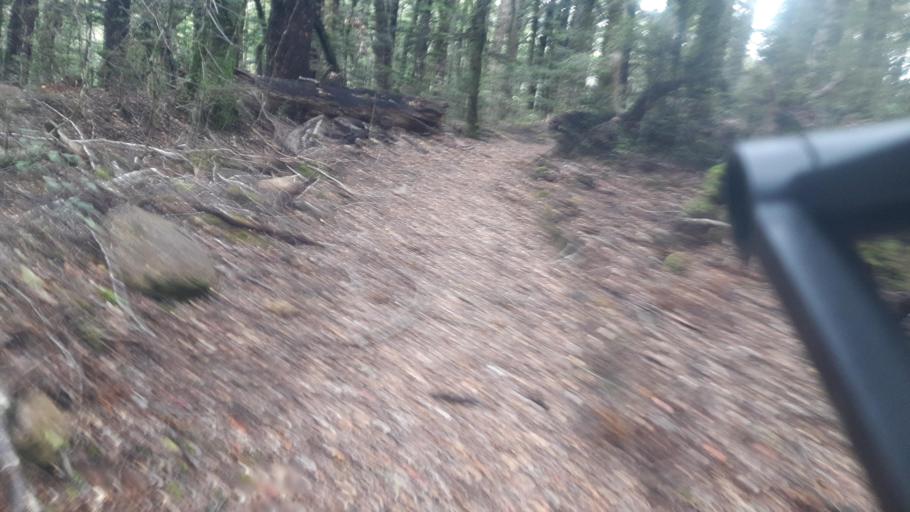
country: NZ
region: Tasman
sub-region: Tasman District
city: Wakefield
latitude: -41.7625
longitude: 172.8110
